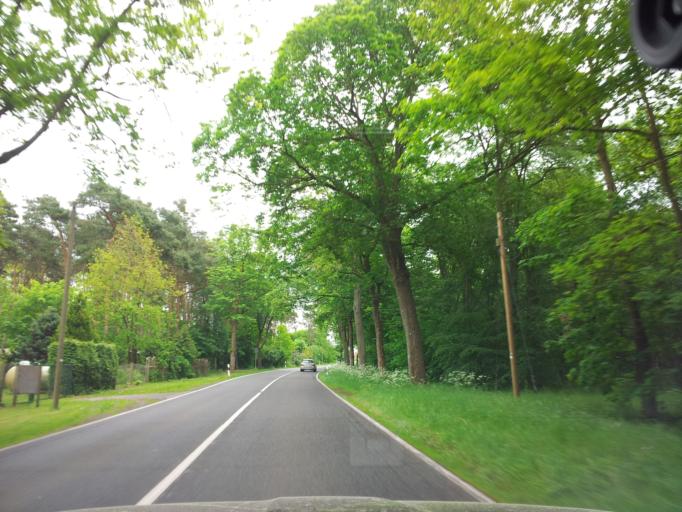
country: DE
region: Brandenburg
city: Brieselang
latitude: 52.6077
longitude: 13.0299
